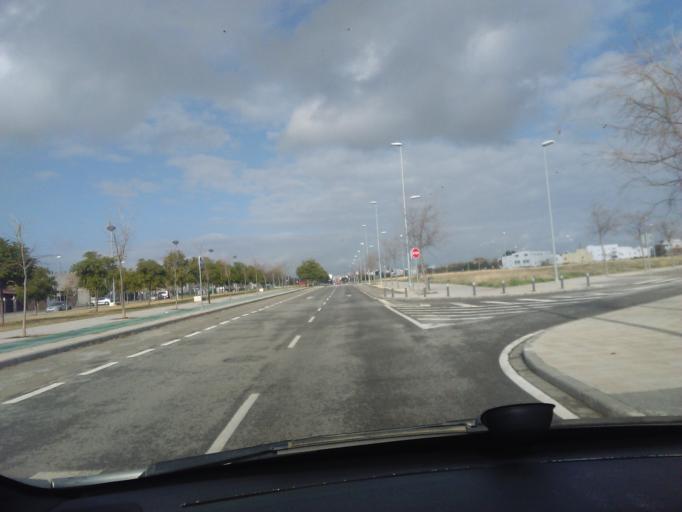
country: ES
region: Andalusia
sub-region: Provincia de Sevilla
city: Sevilla
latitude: 37.3789
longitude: -5.9143
